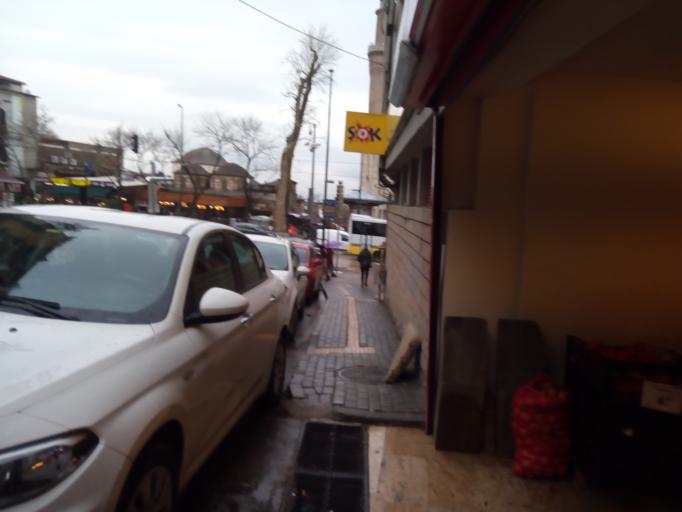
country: TR
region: Bursa
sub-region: Osmangazi
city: Bursa
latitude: 40.1831
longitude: 29.0615
